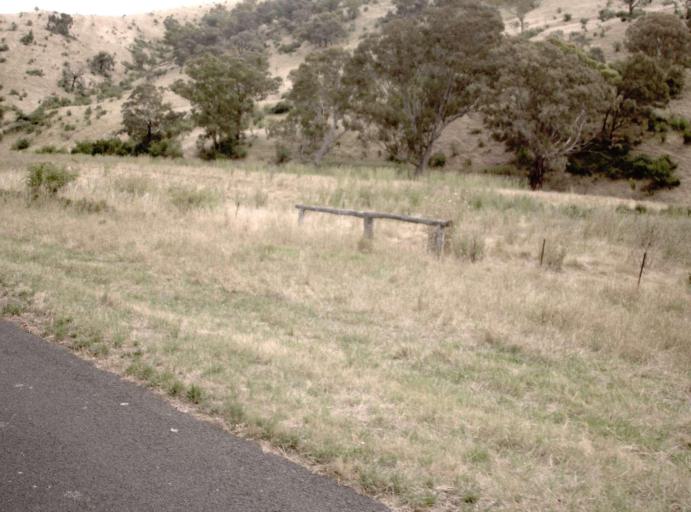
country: AU
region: Victoria
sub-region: Wellington
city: Heyfield
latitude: -37.6403
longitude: 146.6364
